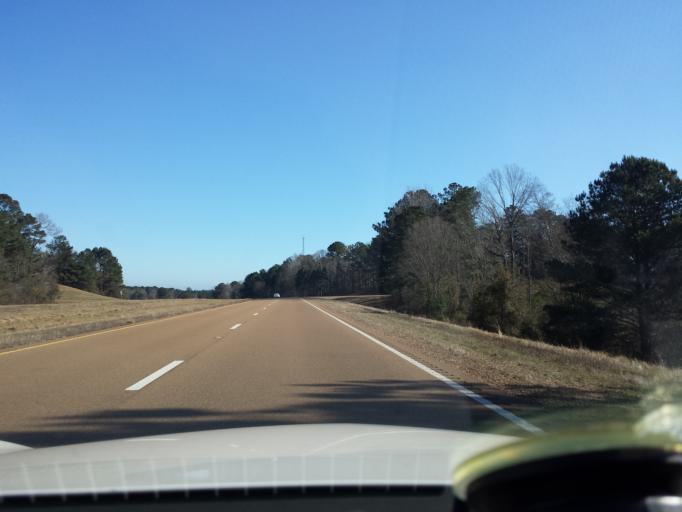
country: US
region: Mississippi
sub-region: Leake County
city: Carthage
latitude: 32.6384
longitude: -89.6612
